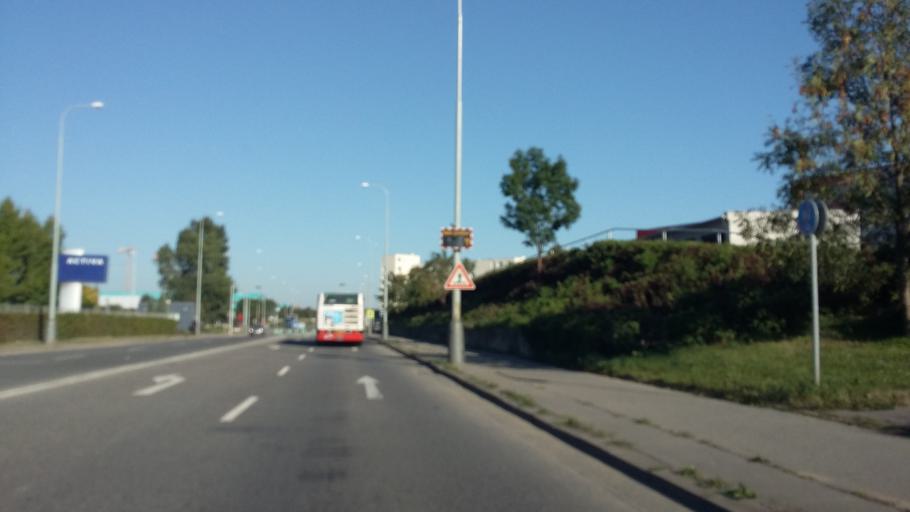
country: CZ
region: Praha
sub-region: Praha 18
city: Letnany
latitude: 50.1421
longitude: 14.5125
